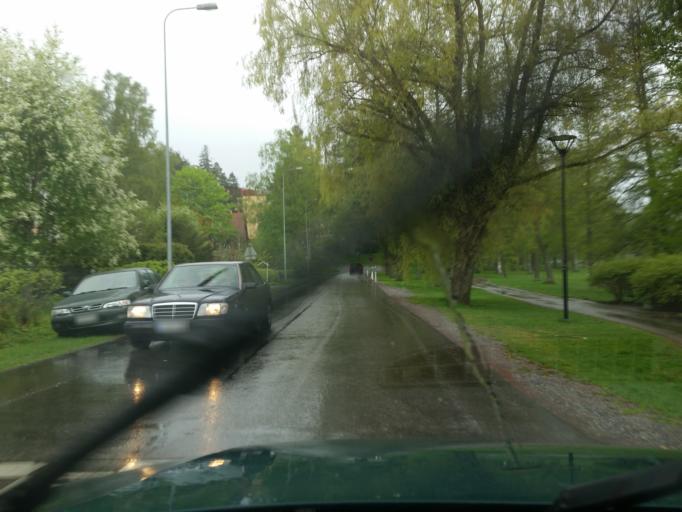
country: FI
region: Uusimaa
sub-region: Helsinki
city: Lohja
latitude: 60.2484
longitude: 24.0551
